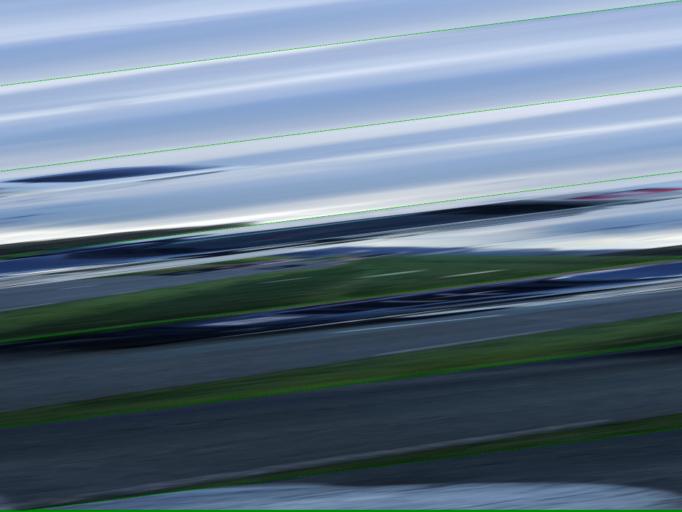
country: FR
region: Picardie
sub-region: Departement de l'Oise
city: Chaumont-en-Vexin
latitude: 49.3237
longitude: 1.8957
